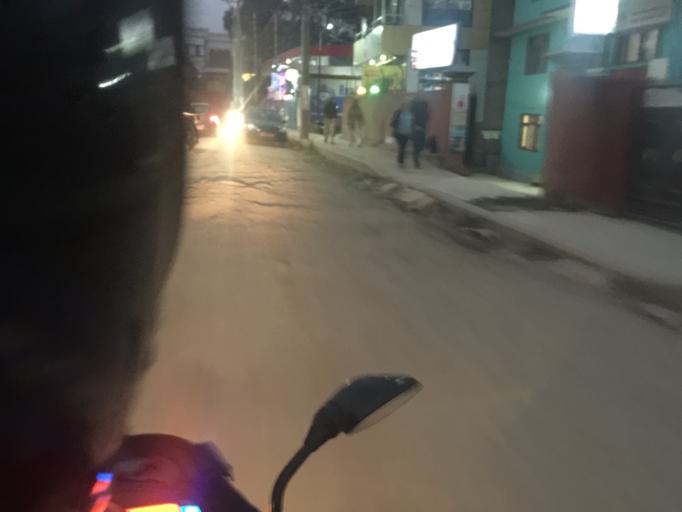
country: NP
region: Central Region
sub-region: Bagmati Zone
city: Patan
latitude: 27.6789
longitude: 85.3079
